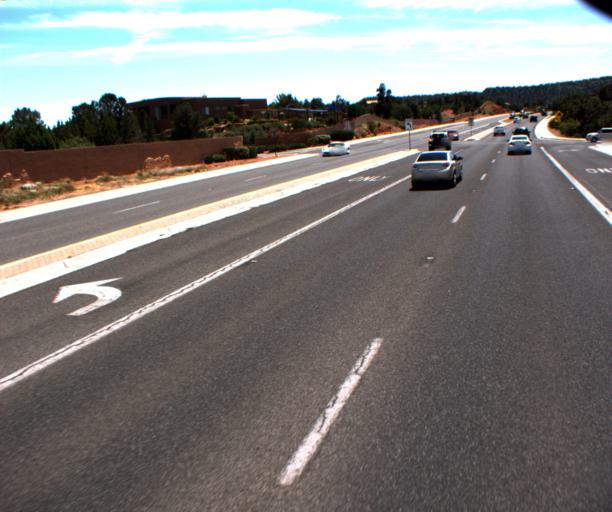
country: US
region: Arizona
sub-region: Yavapai County
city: West Sedona
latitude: 34.8568
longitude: -111.8219
